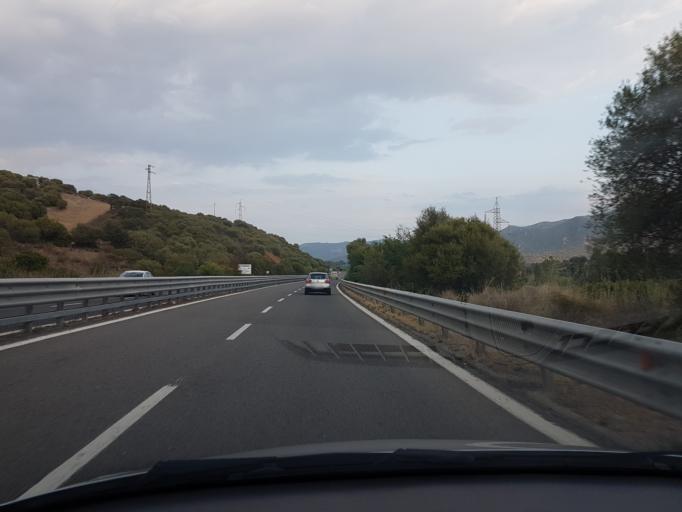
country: IT
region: Sardinia
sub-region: Provincia di Nuoro
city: Orune
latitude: 40.3685
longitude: 9.3774
